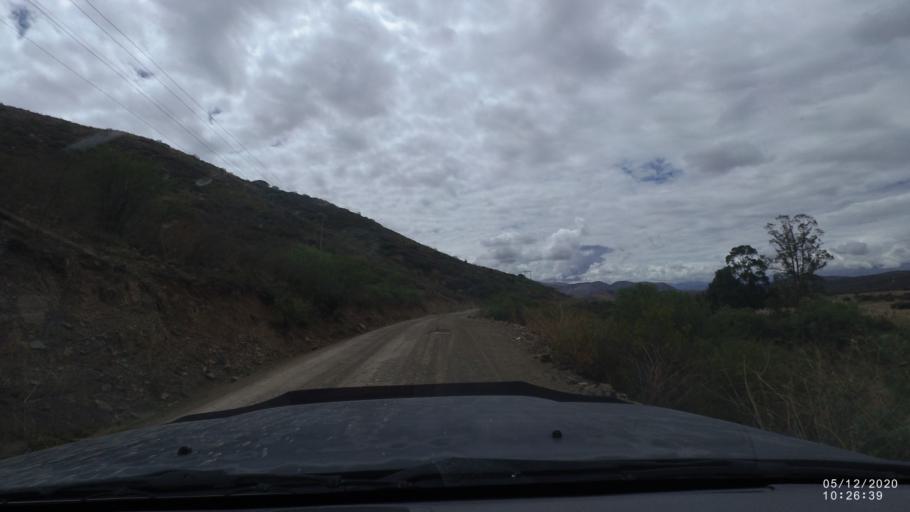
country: BO
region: Cochabamba
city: Sipe Sipe
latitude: -17.5275
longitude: -66.2818
